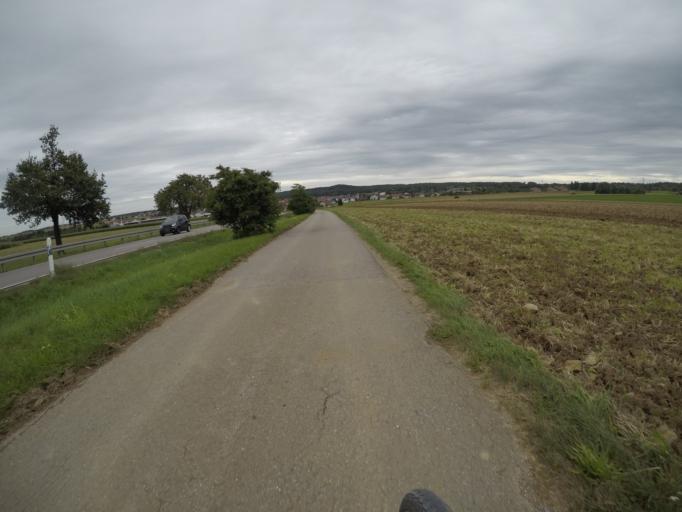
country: DE
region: Baden-Wuerttemberg
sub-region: Regierungsbezirk Stuttgart
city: Hildrizhausen
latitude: 48.6296
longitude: 8.9585
